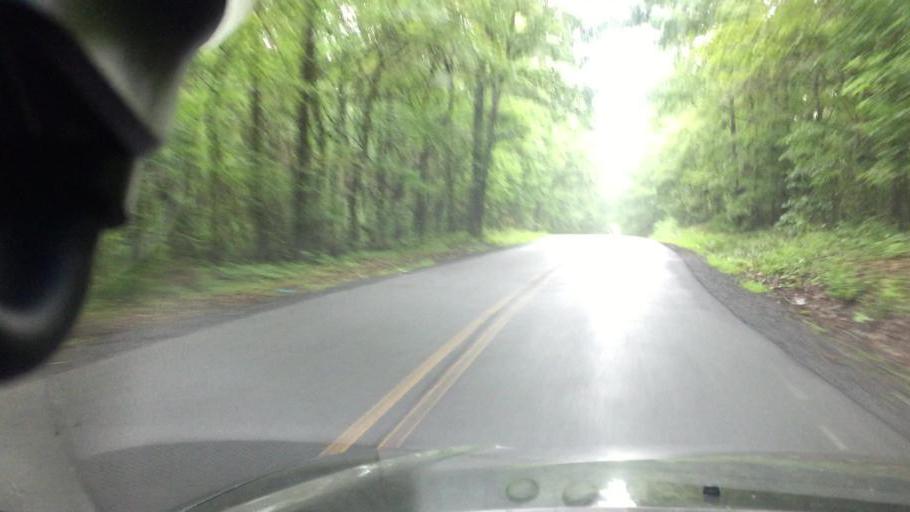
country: US
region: Pennsylvania
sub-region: Luzerne County
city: Freeland
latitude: 41.0231
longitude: -75.9099
